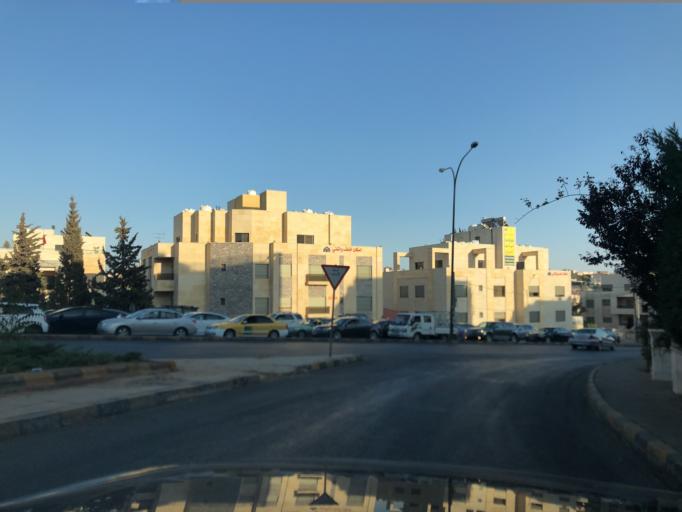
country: JO
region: Amman
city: Wadi as Sir
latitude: 31.9463
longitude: 35.8698
